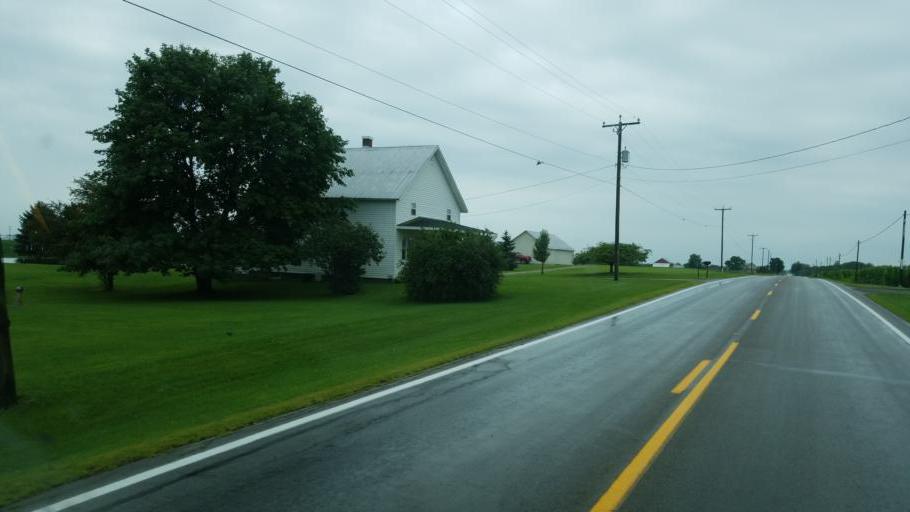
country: US
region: Ohio
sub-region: Hardin County
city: Kenton
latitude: 40.5317
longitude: -83.5381
